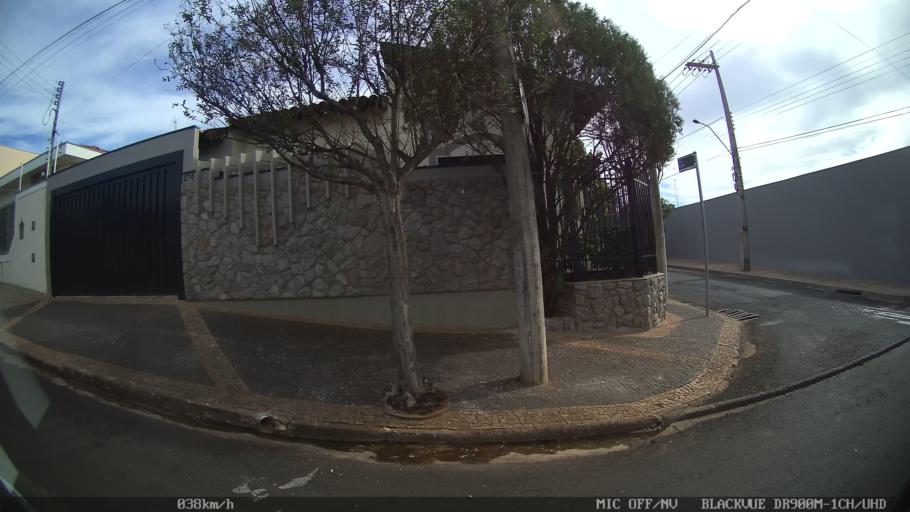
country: BR
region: Sao Paulo
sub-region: Catanduva
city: Catanduva
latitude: -21.1450
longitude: -48.9816
